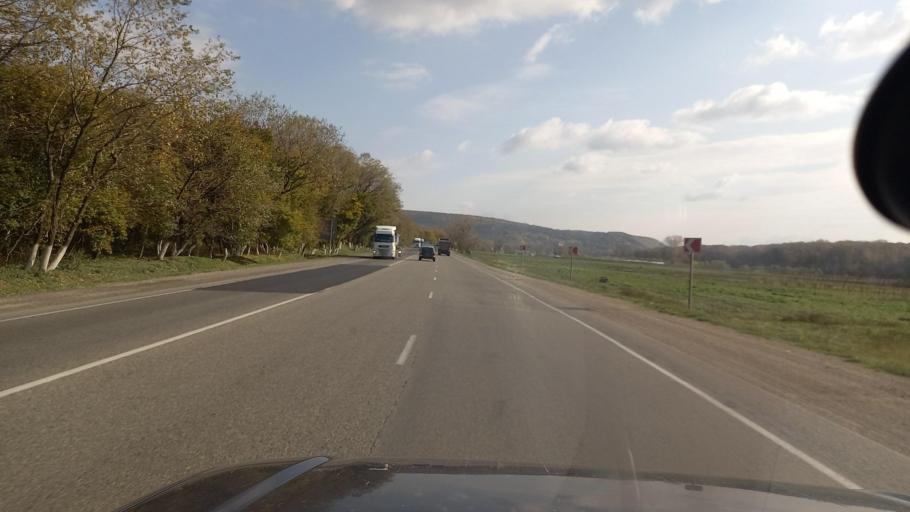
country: RU
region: Krasnodarskiy
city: Gayduk
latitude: 44.8708
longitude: 37.8174
